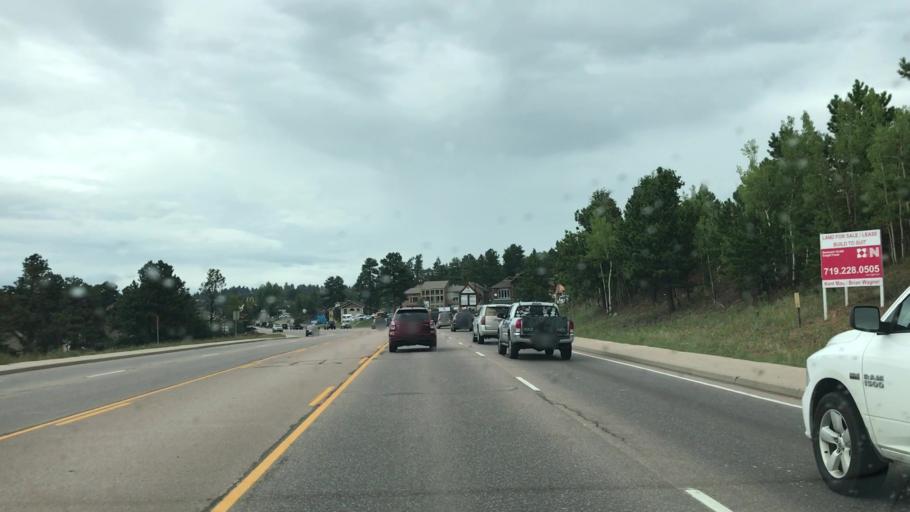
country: US
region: Colorado
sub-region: Teller County
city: Woodland Park
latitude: 38.9857
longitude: -105.0458
